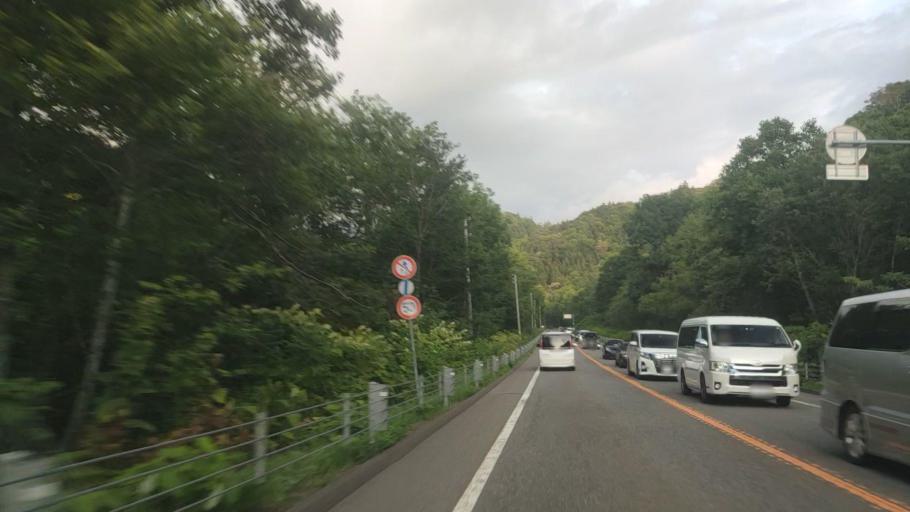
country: JP
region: Hokkaido
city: Utashinai
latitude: 43.2969
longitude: 142.0891
